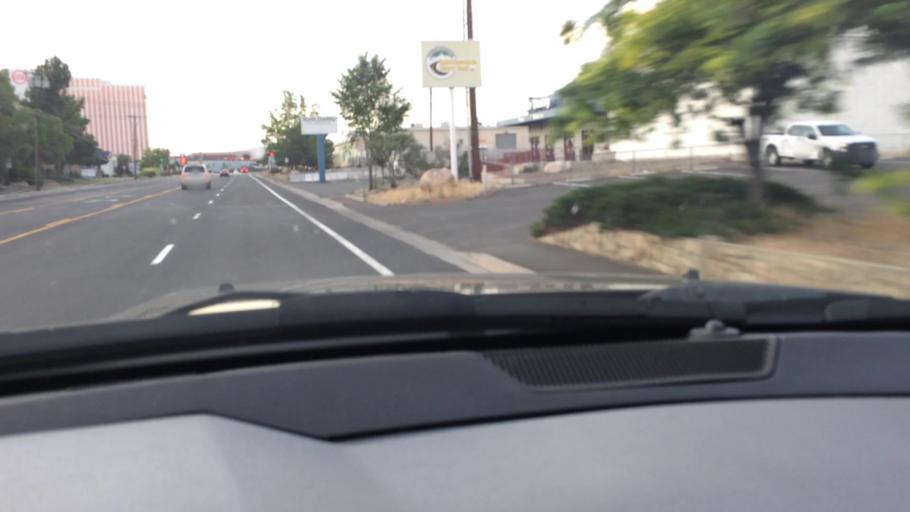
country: US
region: Nevada
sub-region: Washoe County
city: Sparks
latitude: 39.5143
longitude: -119.7774
